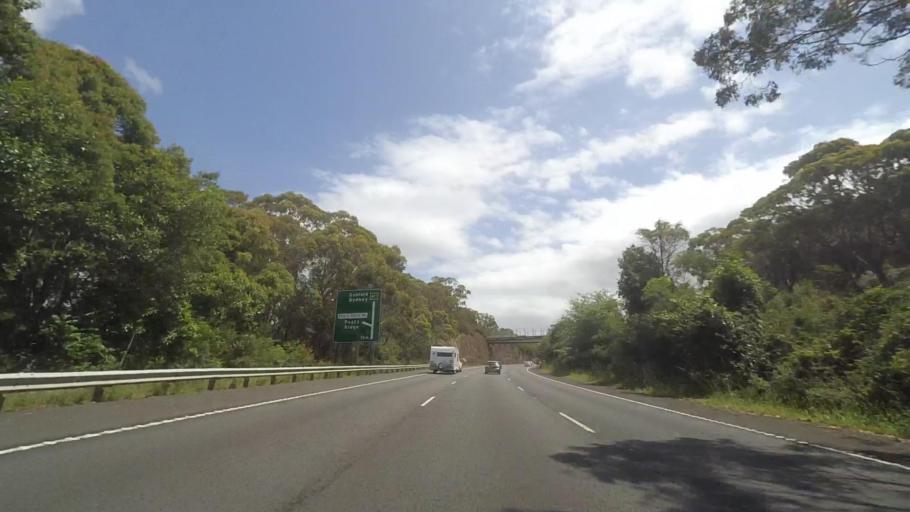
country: AU
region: New South Wales
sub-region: Gosford Shire
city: Lisarow
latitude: -33.3641
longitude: 151.3333
